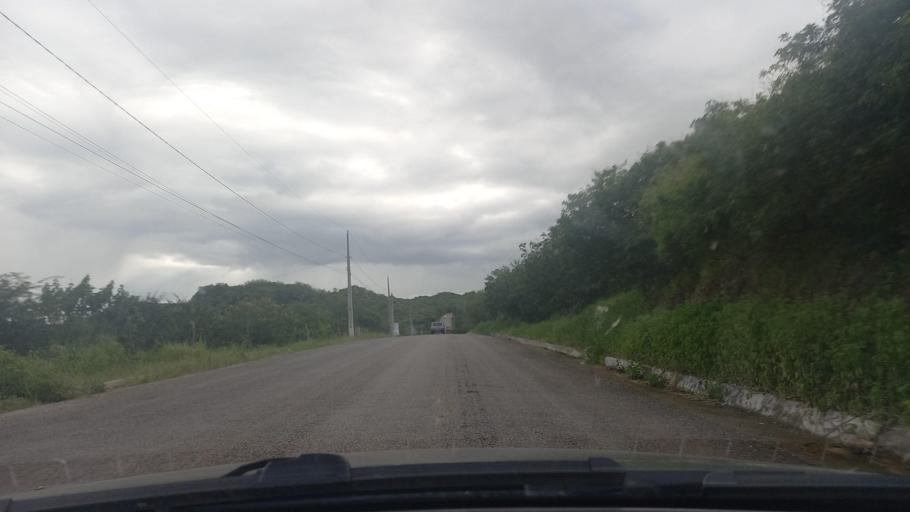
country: BR
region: Sergipe
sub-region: Caninde De Sao Francisco
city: Caninde de Sao Francisco
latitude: -9.6327
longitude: -37.7755
